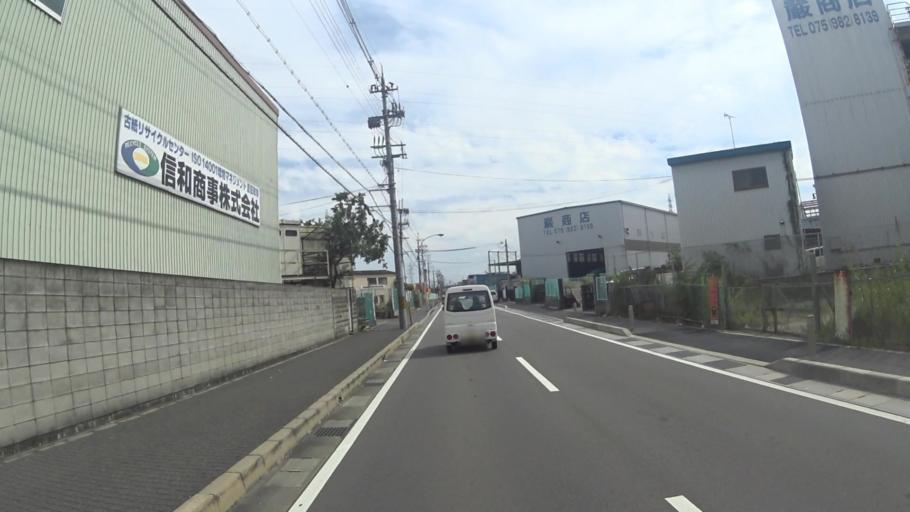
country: JP
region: Kyoto
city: Yawata
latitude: 34.8623
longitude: 135.7078
